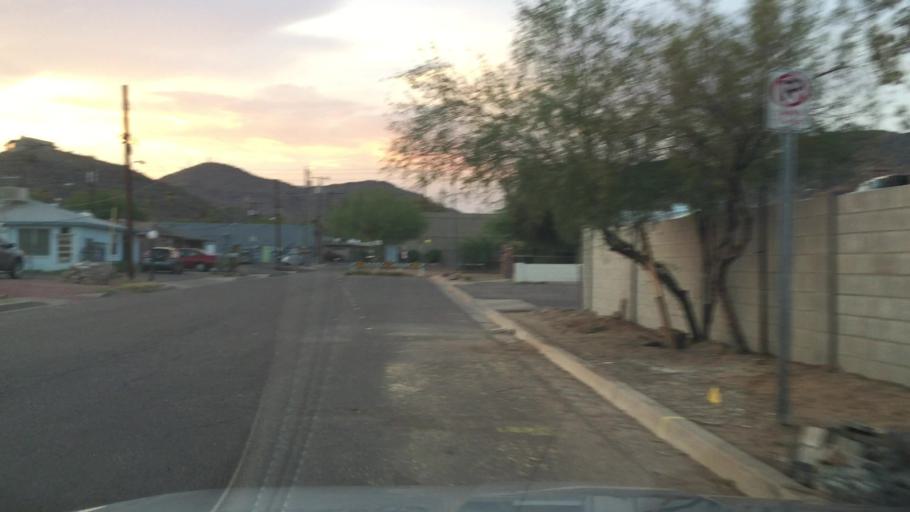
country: US
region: Arizona
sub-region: Maricopa County
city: Glendale
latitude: 33.5700
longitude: -112.0809
